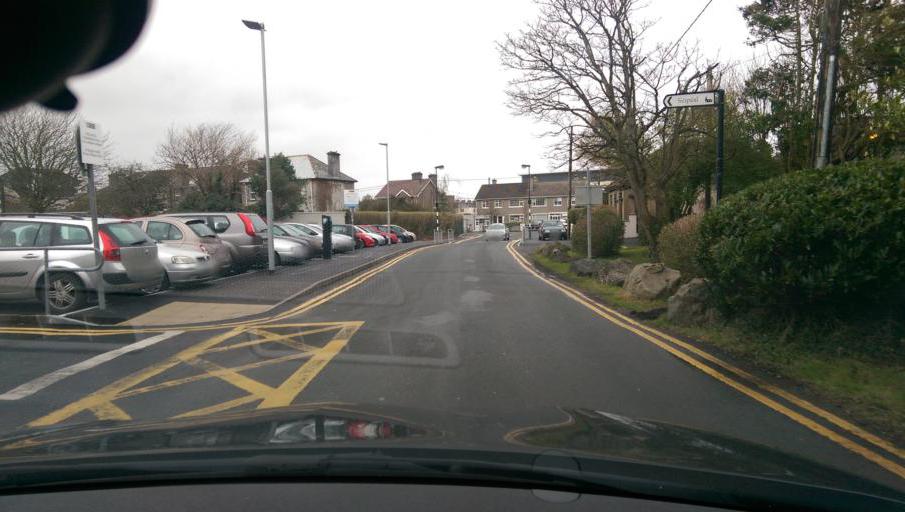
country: IE
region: Connaught
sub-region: County Galway
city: Gaillimh
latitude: 53.2805
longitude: -9.0622
